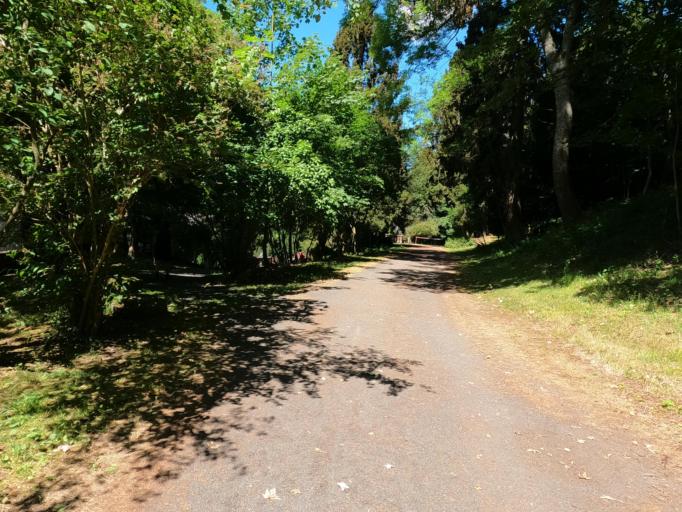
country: DE
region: Hesse
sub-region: Regierungsbezirk Darmstadt
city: Schluchtern
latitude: 50.3325
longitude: 9.6135
